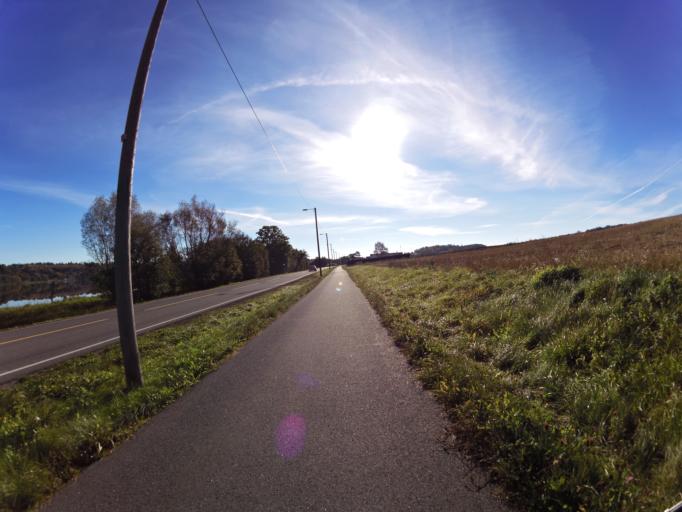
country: NO
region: Ostfold
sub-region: Fredrikstad
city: Fredrikstad
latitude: 59.2854
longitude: 11.0067
